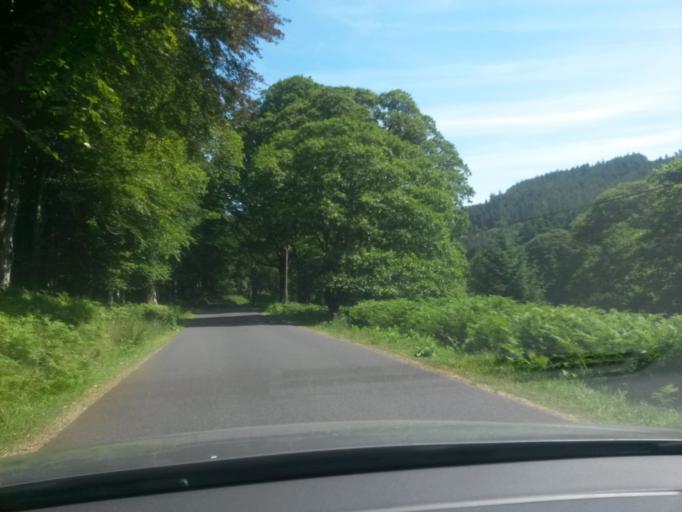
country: IE
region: Leinster
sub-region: Wicklow
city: Enniskerry
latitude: 53.1532
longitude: -6.1989
